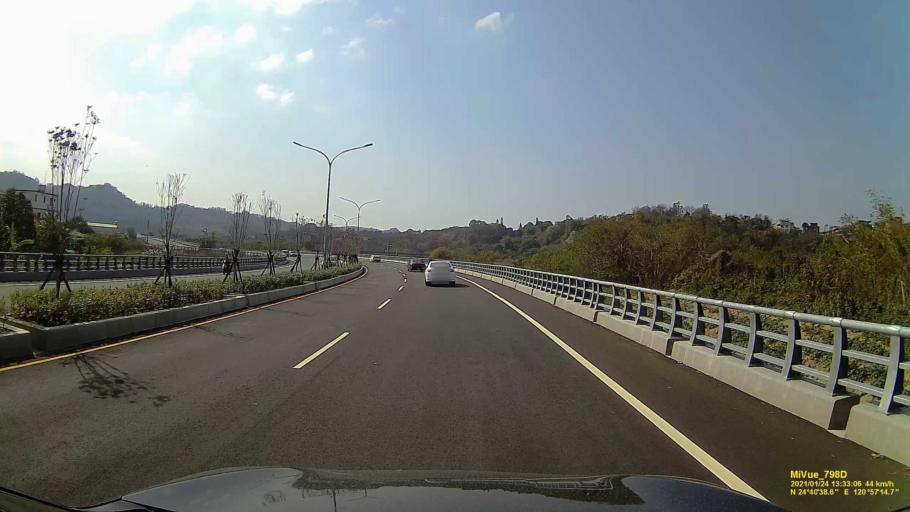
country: TW
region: Taiwan
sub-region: Hsinchu
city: Hsinchu
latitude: 24.6771
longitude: 120.9541
